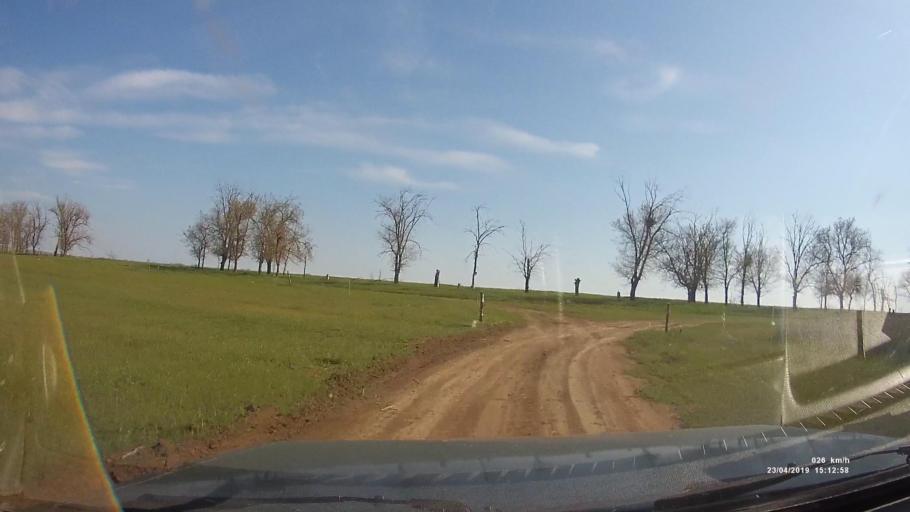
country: RU
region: Rostov
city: Remontnoye
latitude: 46.5404
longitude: 42.9531
